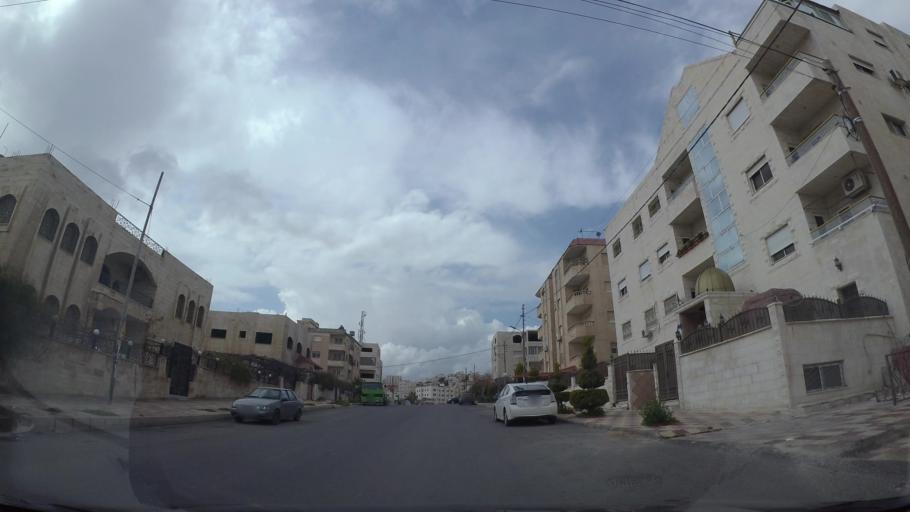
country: JO
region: Amman
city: Amman
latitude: 31.9962
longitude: 35.9418
